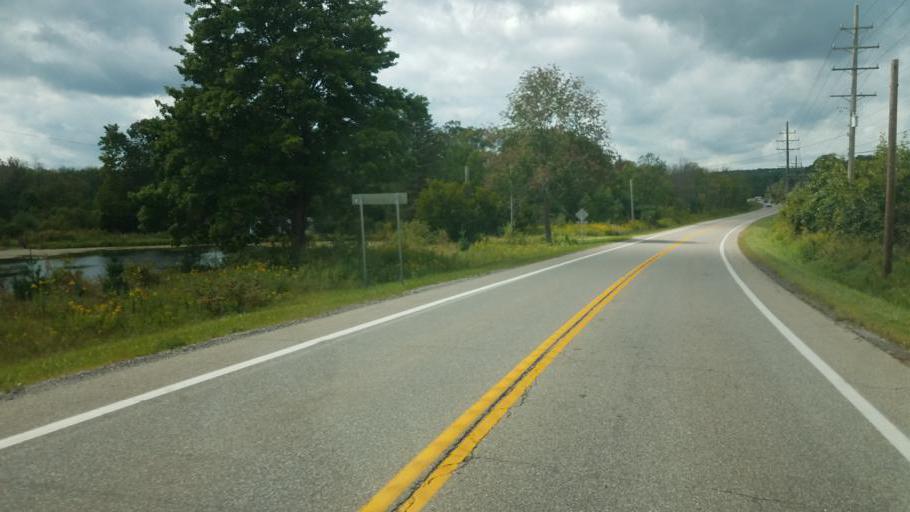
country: US
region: Ohio
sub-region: Geauga County
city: Burton
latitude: 41.5322
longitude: -81.1646
